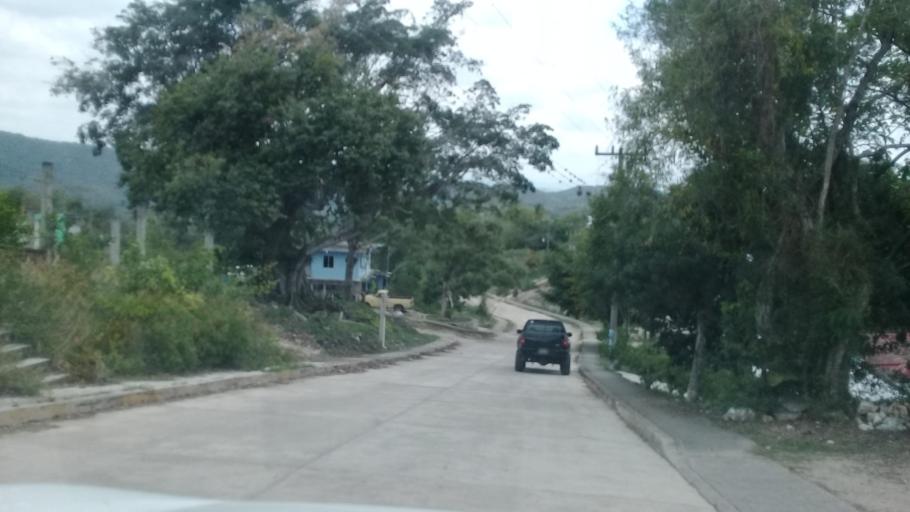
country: MX
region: Veracruz
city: Jalcomulco
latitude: 19.3898
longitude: -96.7920
